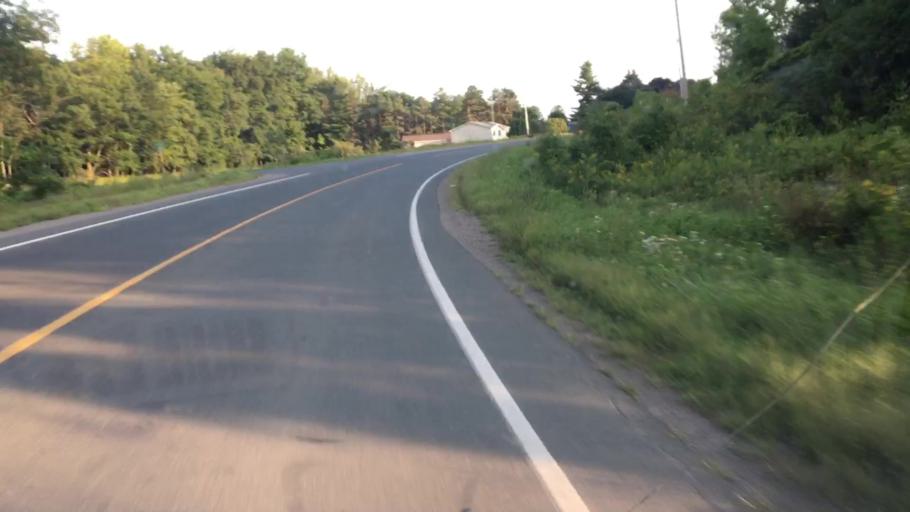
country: CA
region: Ontario
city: Quinte West
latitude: 44.0938
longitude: -77.7324
